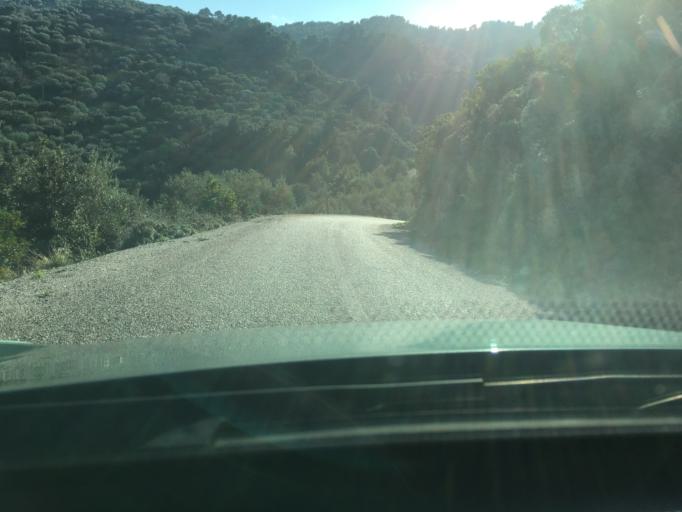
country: GR
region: Thessaly
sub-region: Nomos Magnisias
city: Skopelos
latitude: 39.1784
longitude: 23.6355
